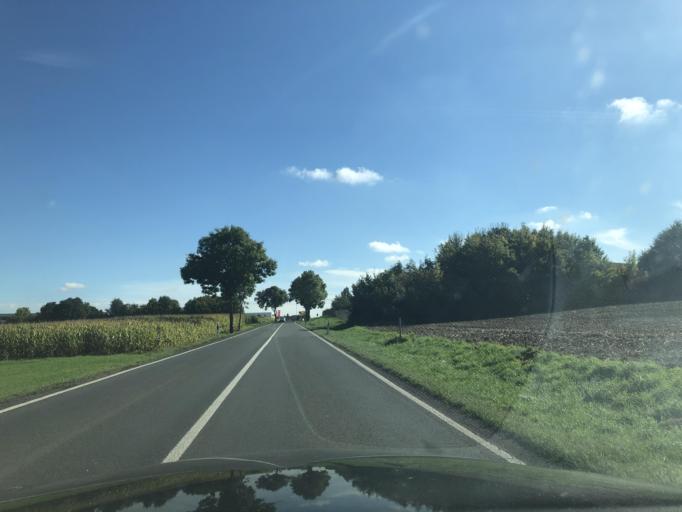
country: DE
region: Thuringia
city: Crimla
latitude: 50.7805
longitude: 12.0350
